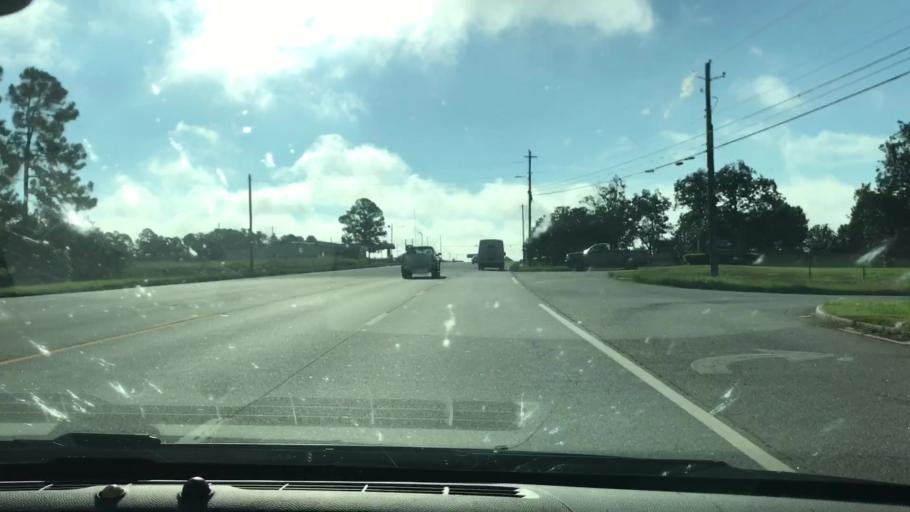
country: US
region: Georgia
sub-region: Terrell County
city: Dawson
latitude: 31.7610
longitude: -84.4360
